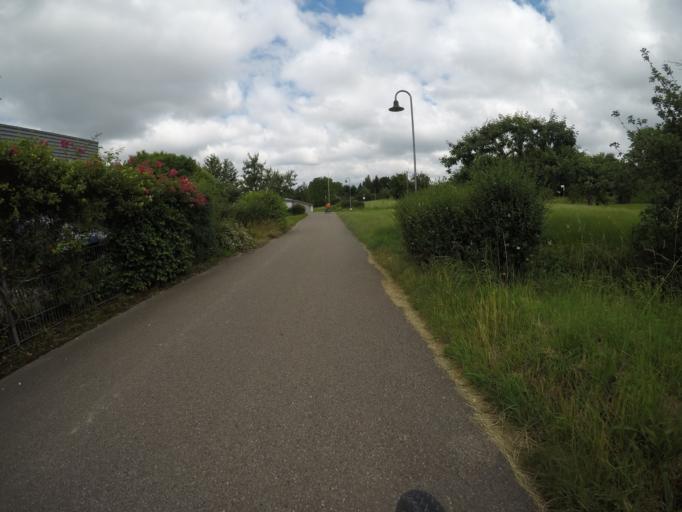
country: DE
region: Baden-Wuerttemberg
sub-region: Regierungsbezirk Stuttgart
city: Gingen an der Fils
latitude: 48.6700
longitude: 9.7775
